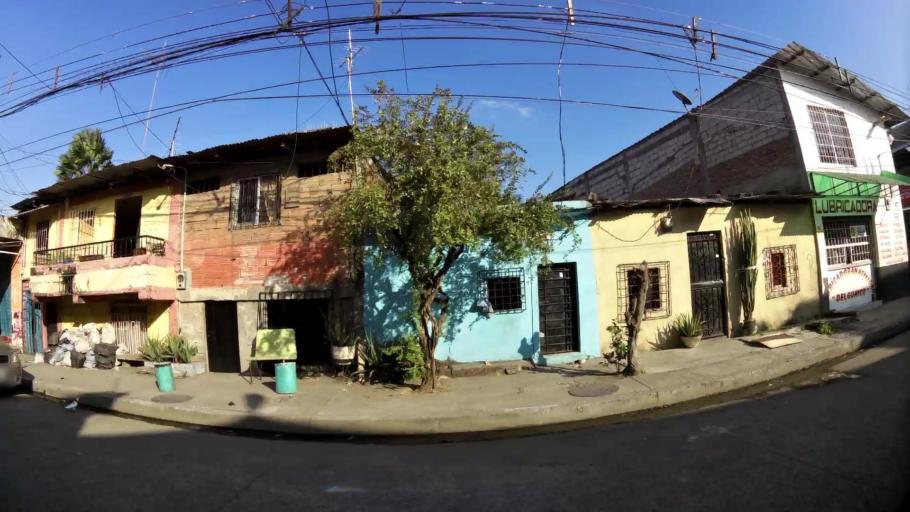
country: EC
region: Guayas
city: Guayaquil
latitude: -2.1555
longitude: -79.9246
